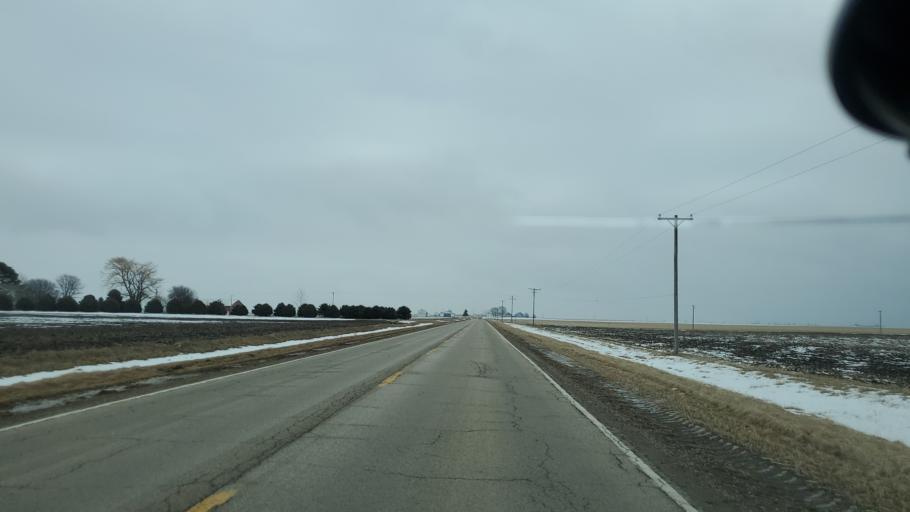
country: US
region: Illinois
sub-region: Marshall County
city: Wenona
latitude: 41.1188
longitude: -89.1074
